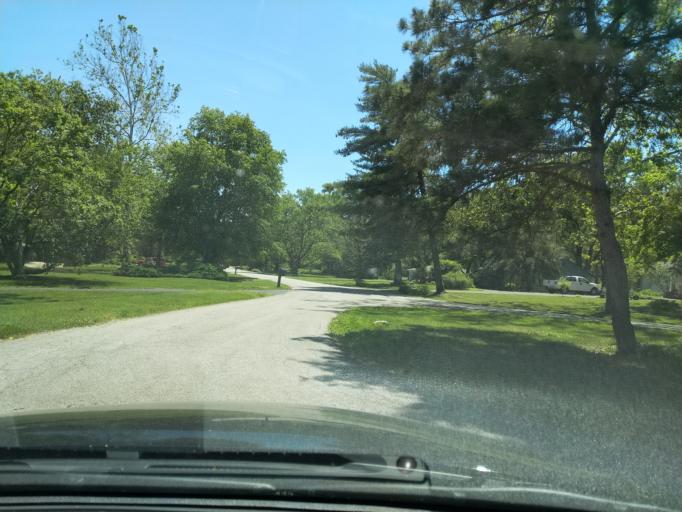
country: US
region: Indiana
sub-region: Hamilton County
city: Carmel
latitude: 39.9440
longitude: -86.1339
